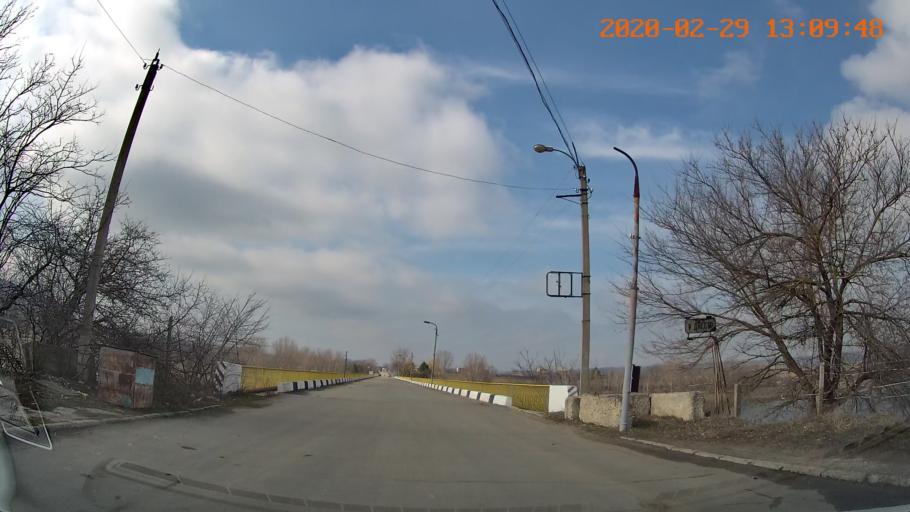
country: MD
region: Telenesti
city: Camenca
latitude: 48.0114
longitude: 28.7031
